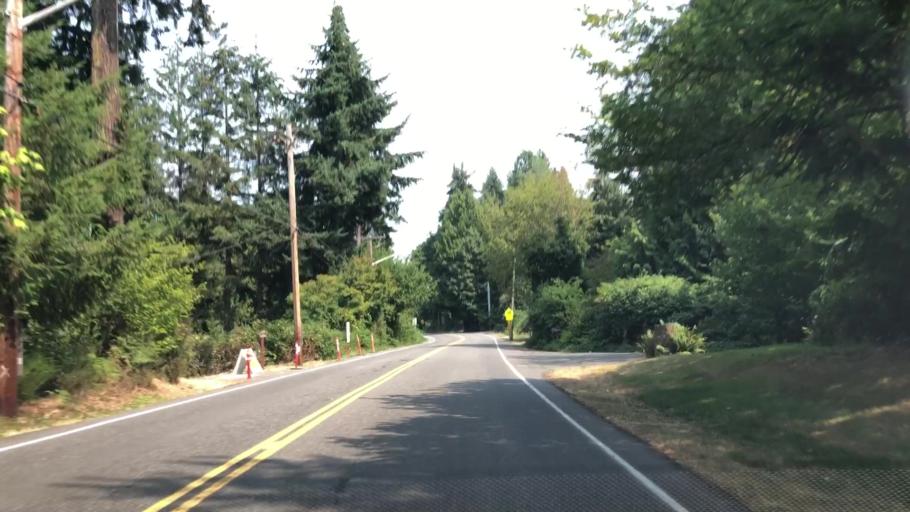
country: US
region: Washington
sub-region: Snohomish County
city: Brier
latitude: 47.7748
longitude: -122.2567
